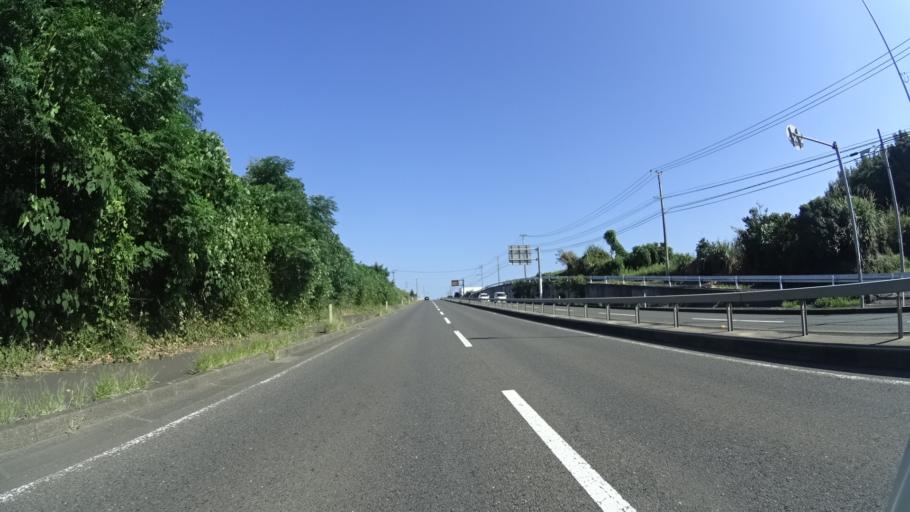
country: JP
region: Fukuoka
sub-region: Buzen-shi
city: Buzen
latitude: 33.6088
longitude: 131.1120
